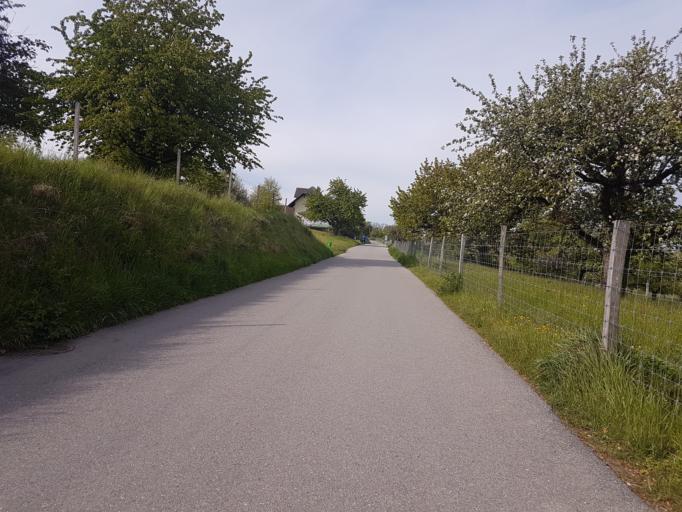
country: CH
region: Bern
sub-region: Biel/Bienne District
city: Bellmund
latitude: 47.1024
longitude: 7.2144
